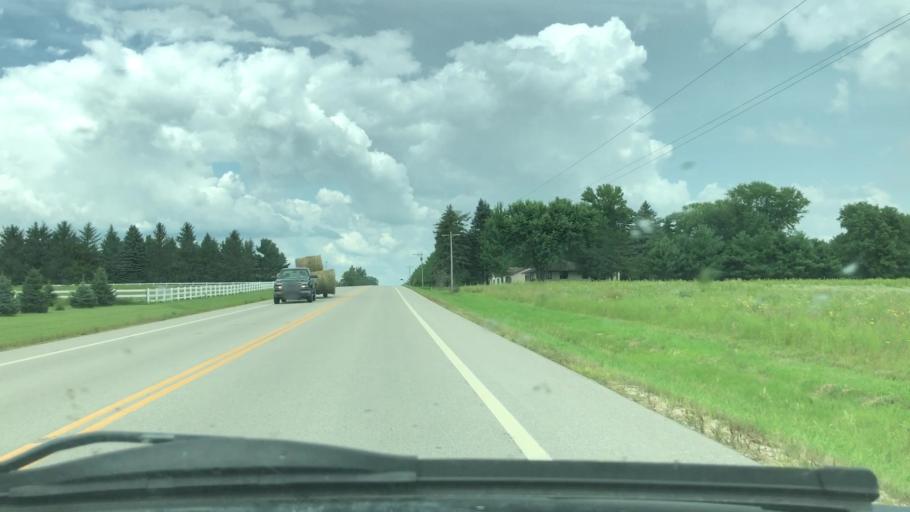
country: US
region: Minnesota
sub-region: Olmsted County
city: Stewartville
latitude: 43.8648
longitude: -92.5287
